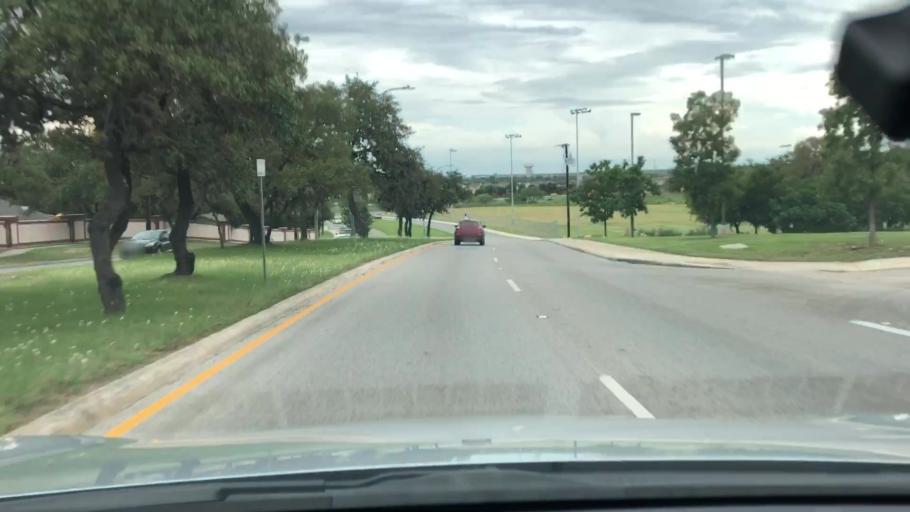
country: US
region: Texas
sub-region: Bexar County
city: Leon Valley
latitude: 29.4762
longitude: -98.6669
